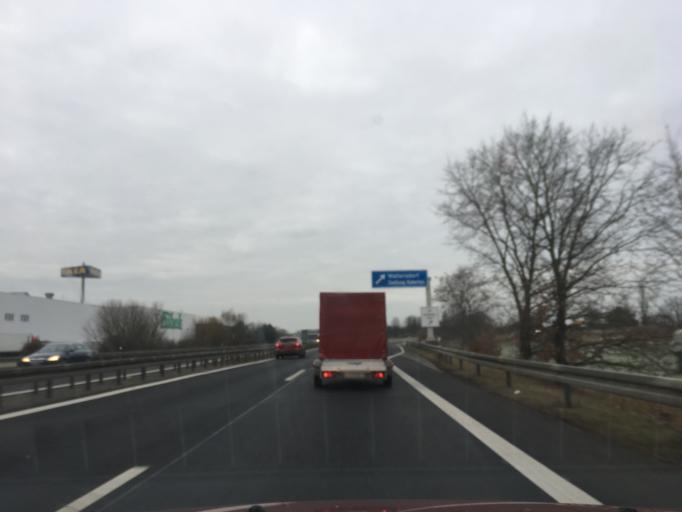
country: DE
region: Brandenburg
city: Schulzendorf
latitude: 52.3703
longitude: 13.5569
